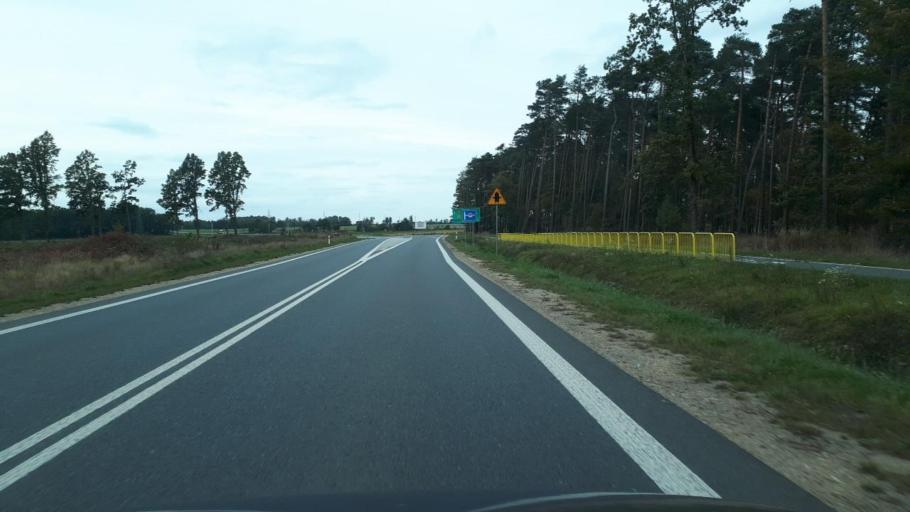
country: PL
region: Opole Voivodeship
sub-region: Powiat oleski
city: Dobrodzien
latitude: 50.7016
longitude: 18.4474
